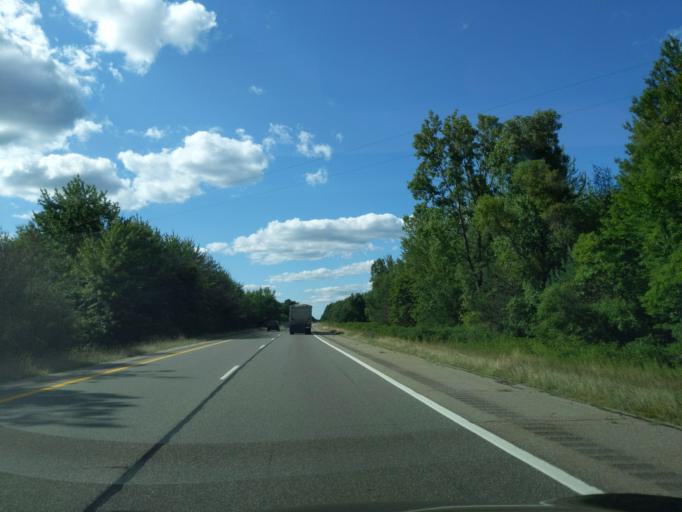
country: US
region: Michigan
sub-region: Muskegon County
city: Fruitport
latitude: 43.1032
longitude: -86.1123
